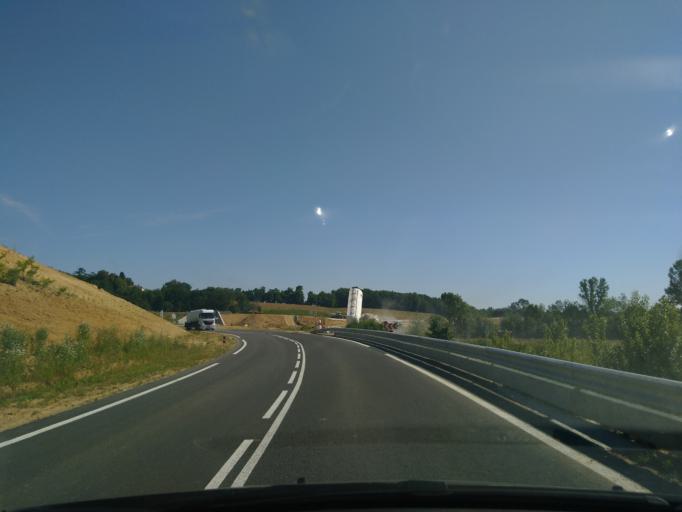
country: FR
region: Midi-Pyrenees
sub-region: Departement du Gers
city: Gimont
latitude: 43.6141
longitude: 0.8554
